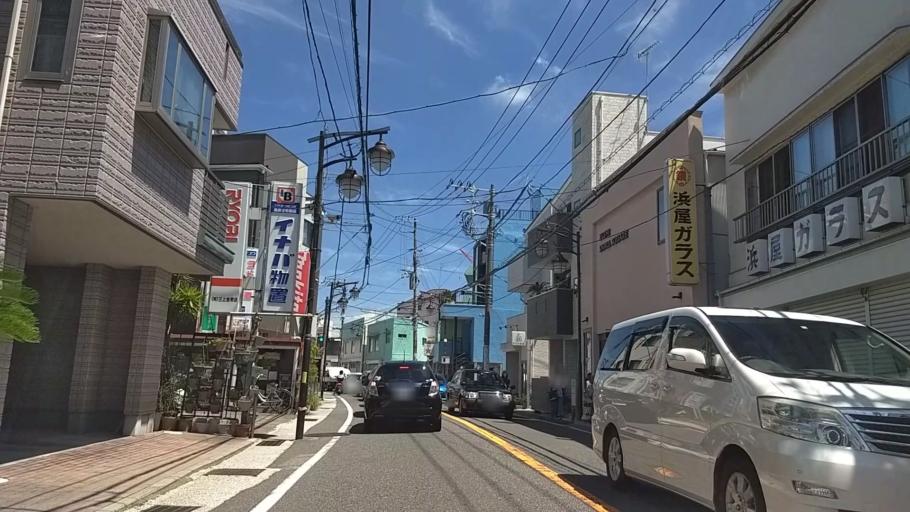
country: JP
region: Kanagawa
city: Zushi
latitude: 35.2970
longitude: 139.5744
